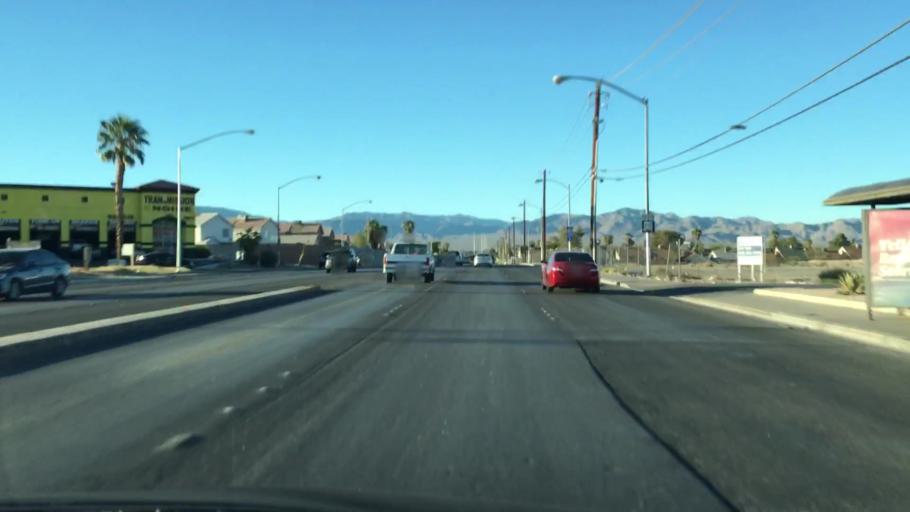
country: US
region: Nevada
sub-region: Clark County
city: Sunrise Manor
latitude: 36.2264
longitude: -115.0801
